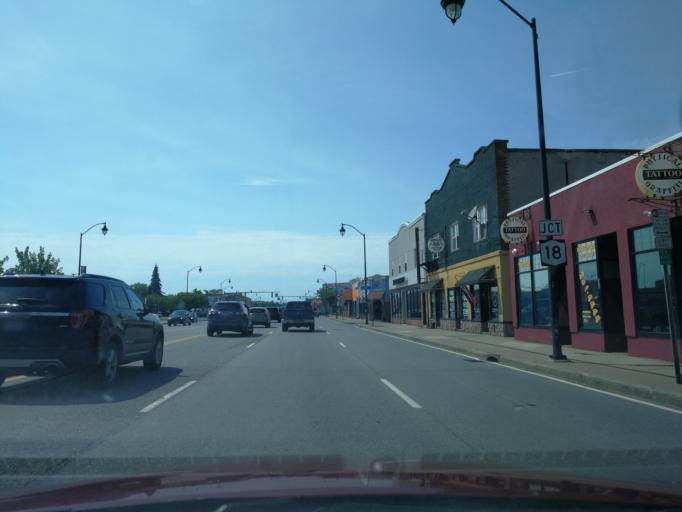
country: US
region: New York
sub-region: Monroe County
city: Rochester
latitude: 43.1998
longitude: -77.6369
